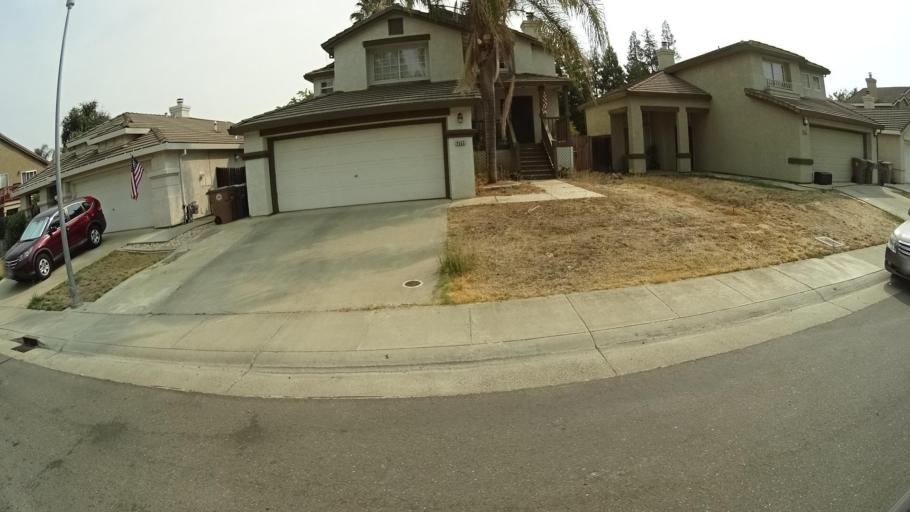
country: US
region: California
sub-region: Sacramento County
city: Laguna
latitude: 38.4116
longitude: -121.4078
